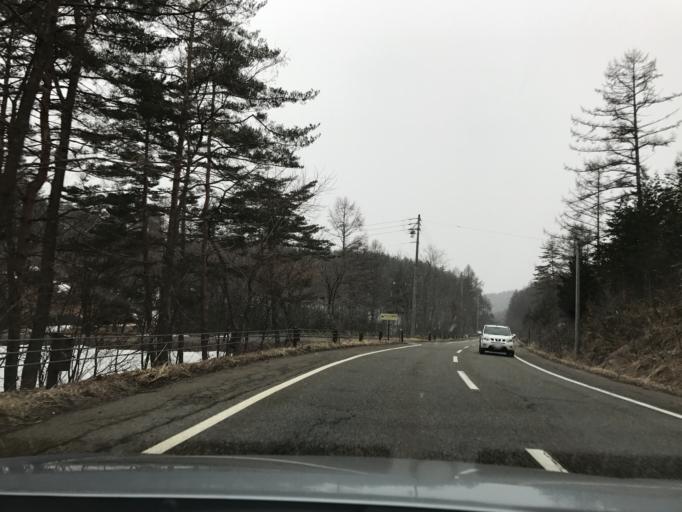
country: JP
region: Nagano
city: Omachi
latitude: 36.5494
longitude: 137.8635
